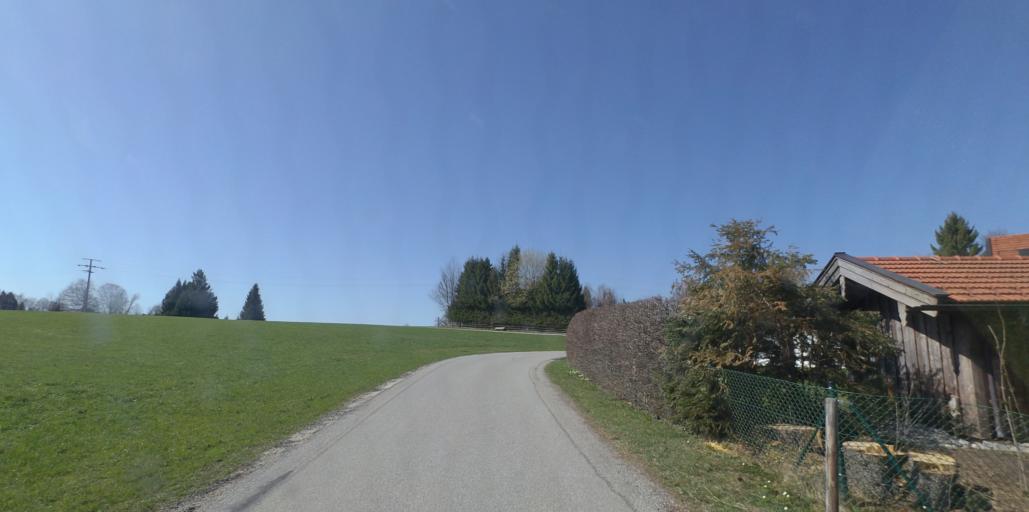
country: DE
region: Bavaria
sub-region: Upper Bavaria
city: Siegsdorf
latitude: 47.8046
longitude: 12.6355
